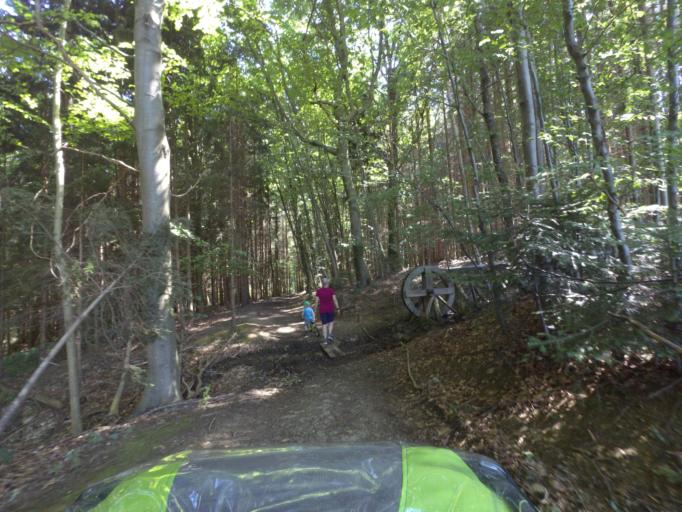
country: AT
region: Salzburg
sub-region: Politischer Bezirk Salzburg-Umgebung
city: Schleedorf
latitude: 47.9828
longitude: 13.1394
